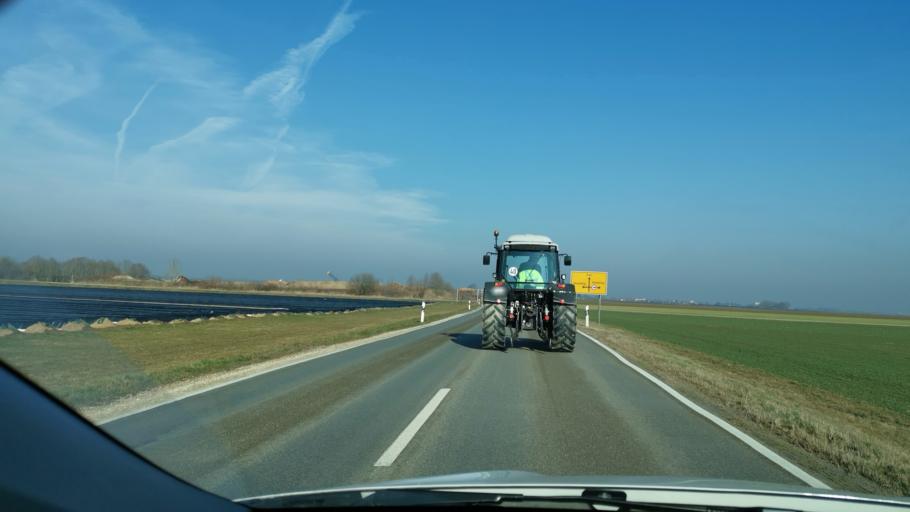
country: DE
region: Bavaria
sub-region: Swabia
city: Rain
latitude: 48.6585
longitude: 10.9205
